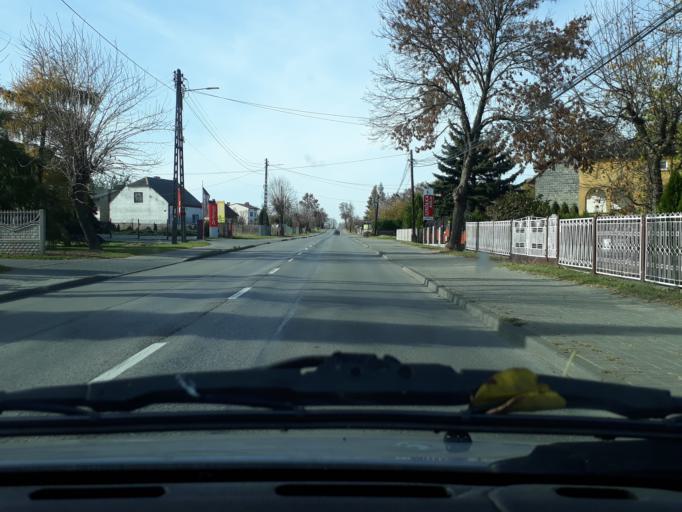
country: PL
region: Silesian Voivodeship
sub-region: Powiat myszkowski
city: Kozieglowy
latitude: 50.5988
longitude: 19.1435
